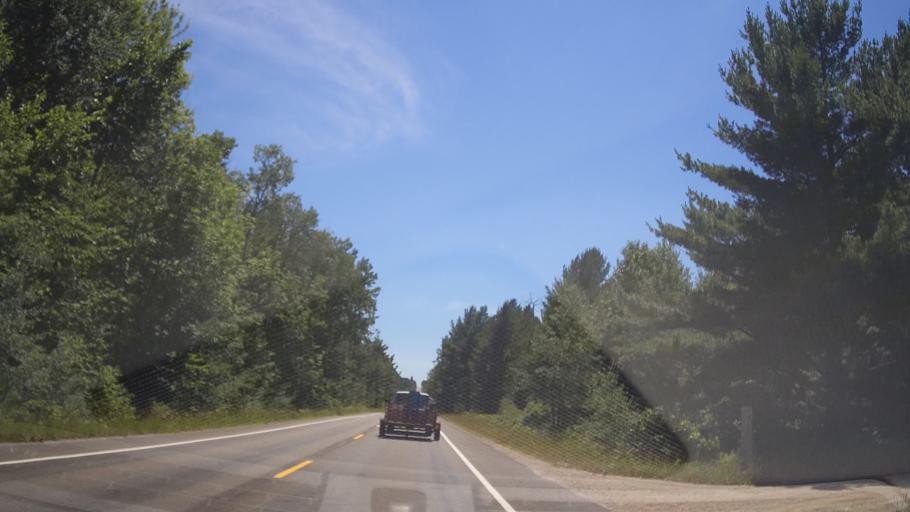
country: US
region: Michigan
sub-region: Grand Traverse County
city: Traverse City
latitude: 44.6357
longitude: -85.6964
